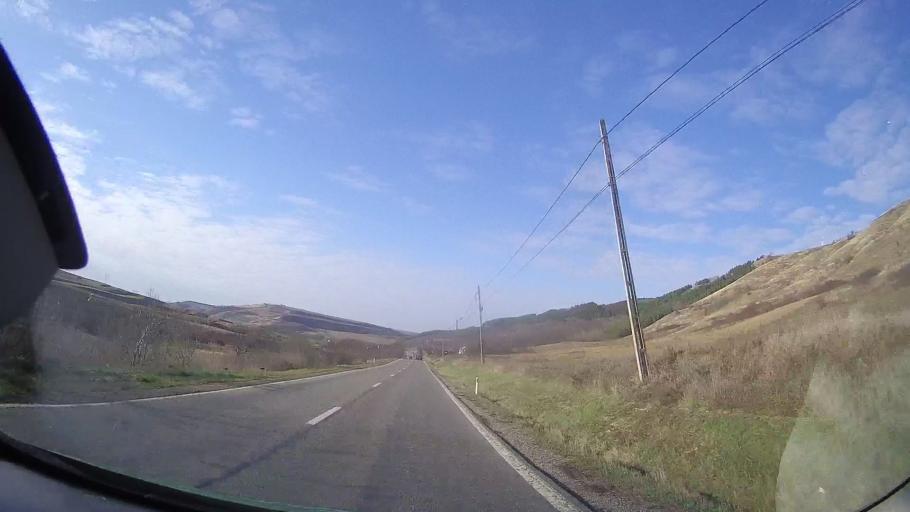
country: RO
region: Cluj
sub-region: Comuna Caianu
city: Vaida-Camaras
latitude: 46.7991
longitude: 23.9455
